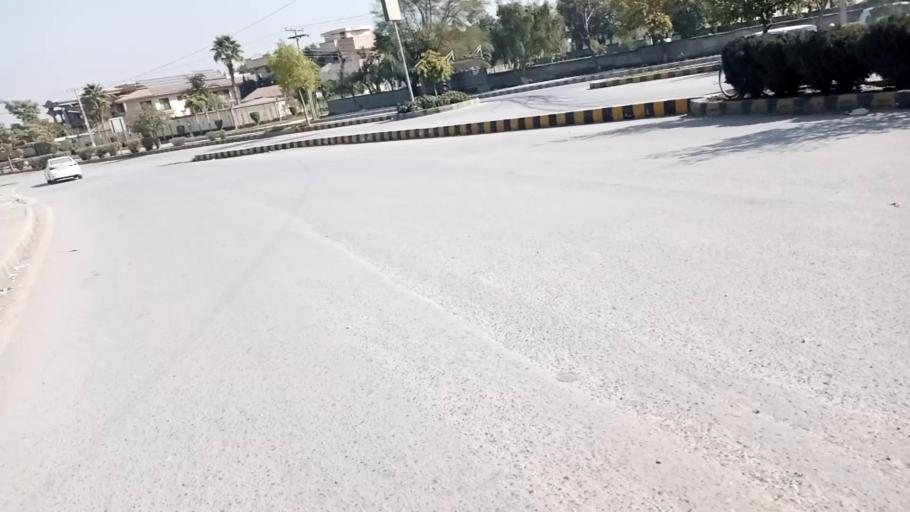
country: PK
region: Khyber Pakhtunkhwa
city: Peshawar
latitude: 33.9640
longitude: 71.4317
